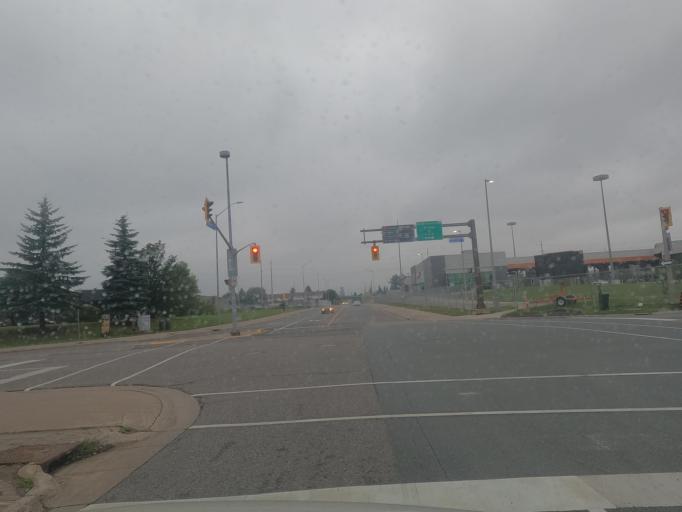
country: CA
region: Ontario
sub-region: Algoma
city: Sault Ste. Marie
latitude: 46.5184
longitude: -84.3476
